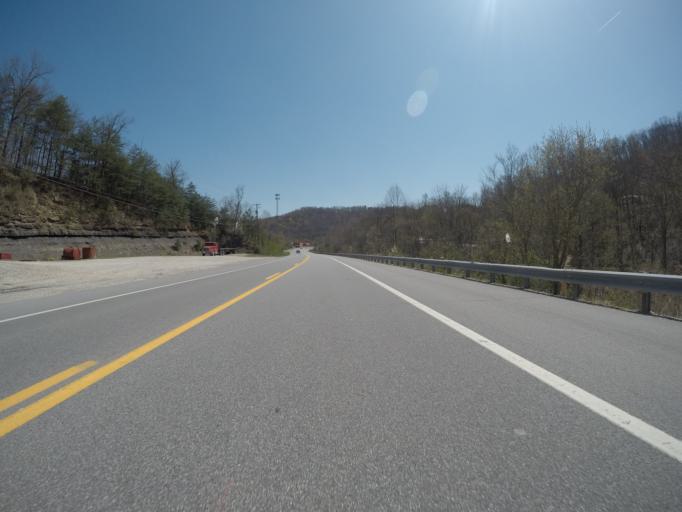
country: US
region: West Virginia
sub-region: Kanawha County
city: Pinch
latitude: 38.4096
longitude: -81.5434
